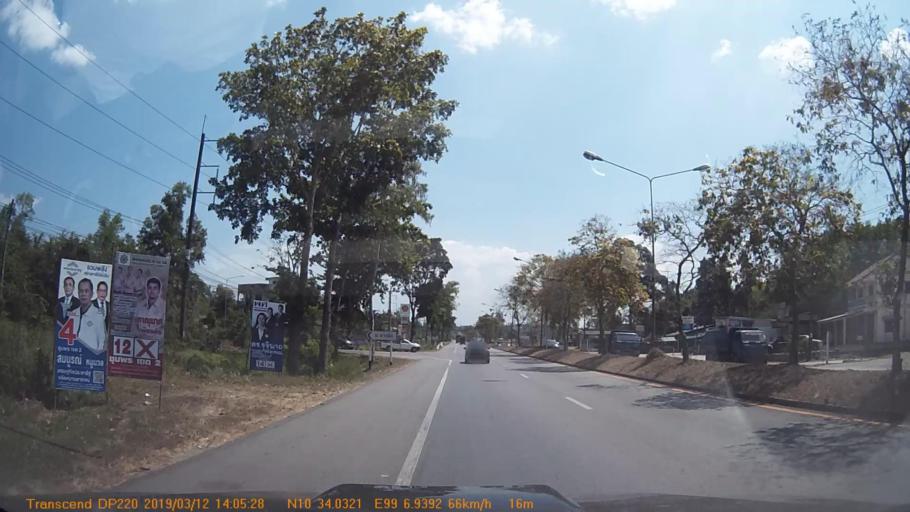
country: TH
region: Chumphon
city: Chumphon
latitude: 10.5669
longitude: 99.1157
